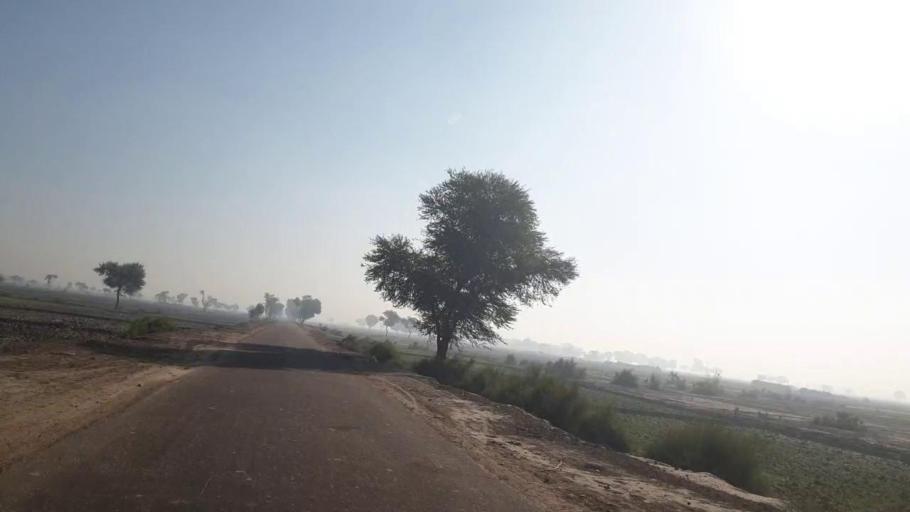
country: PK
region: Sindh
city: Dadu
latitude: 26.6731
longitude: 67.8174
